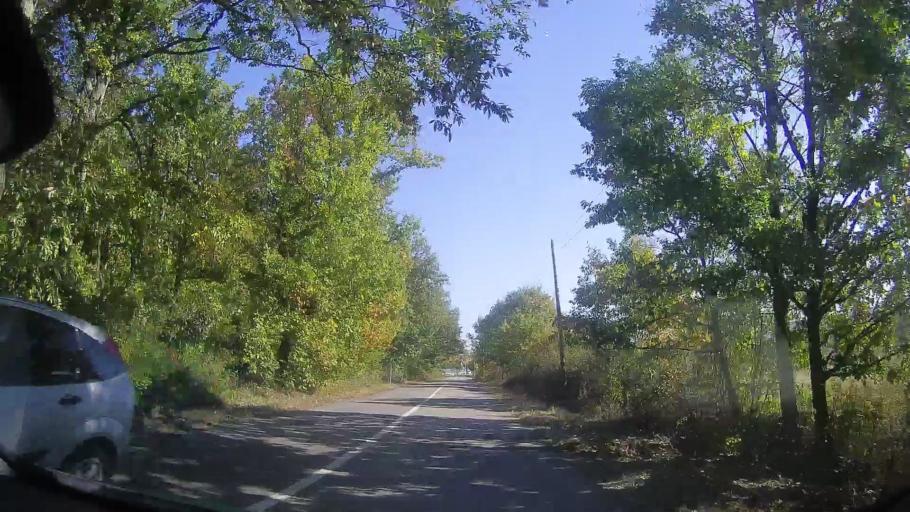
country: RO
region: Timis
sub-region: Comuna Ghizela
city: Ghizela
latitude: 45.8433
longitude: 21.7832
